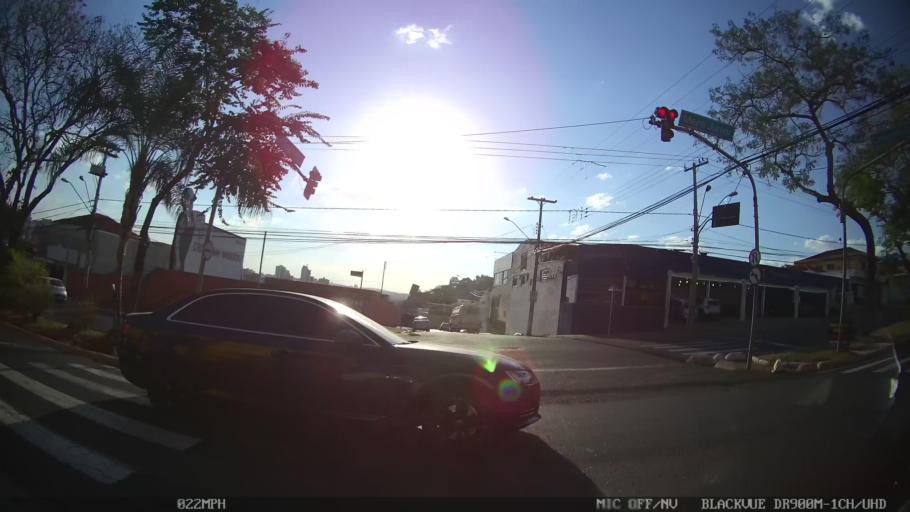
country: BR
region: Sao Paulo
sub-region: Ribeirao Preto
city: Ribeirao Preto
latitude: -21.1776
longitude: -47.7983
